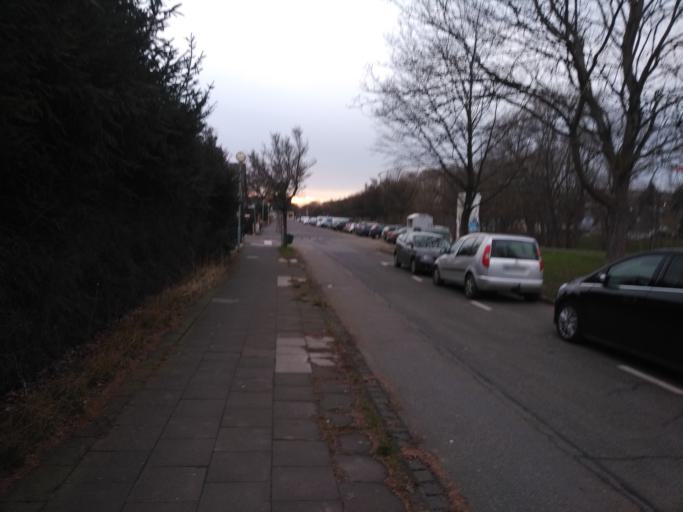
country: DE
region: North Rhine-Westphalia
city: Opladen
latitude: 51.0381
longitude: 7.0077
